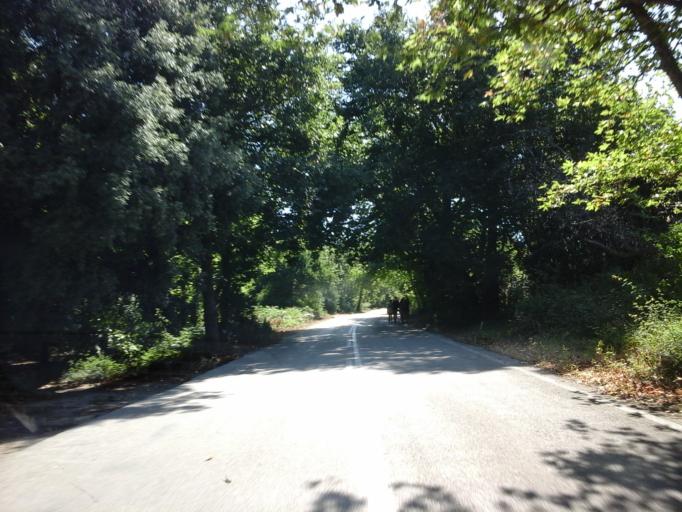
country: GR
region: East Macedonia and Thrace
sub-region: Nomos Evrou
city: Samothraki
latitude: 40.5023
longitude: 25.6086
